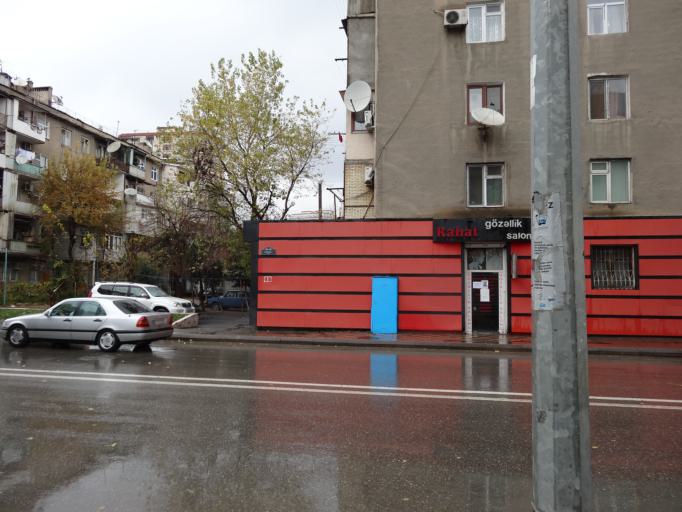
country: AZ
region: Baki
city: Baku
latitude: 40.4004
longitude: 49.8649
